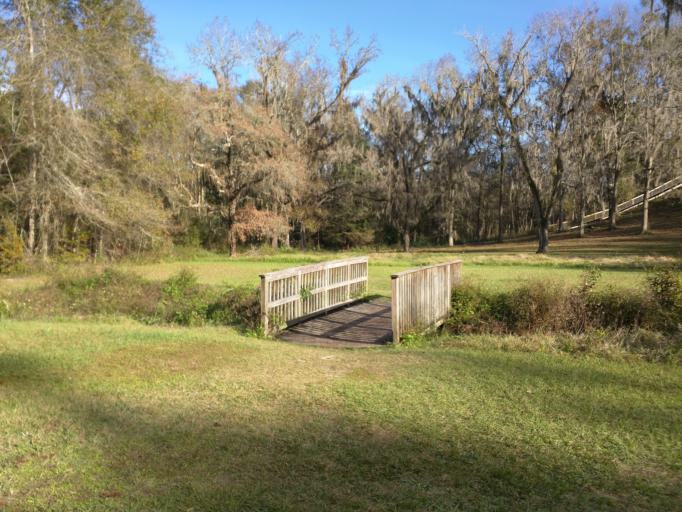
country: US
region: Florida
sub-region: Leon County
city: Tallahassee
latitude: 30.5015
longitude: -84.3126
